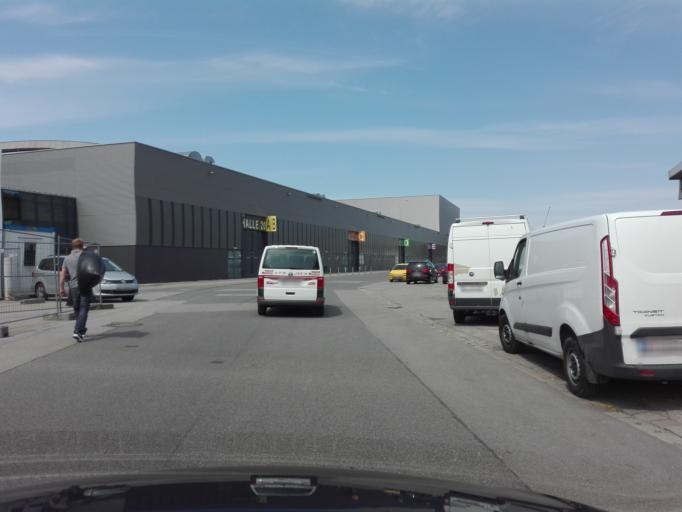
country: AT
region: Upper Austria
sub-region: Wels-Land
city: Thalheim bei Wels
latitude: 48.1504
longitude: 14.0183
